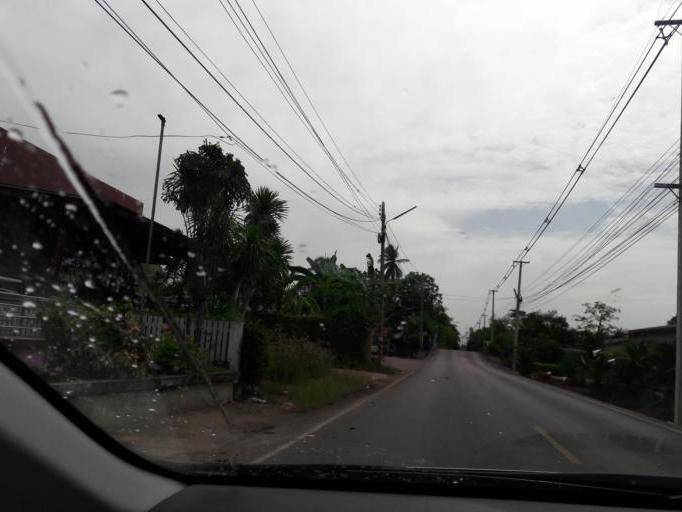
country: TH
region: Ratchaburi
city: Damnoen Saduak
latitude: 13.5368
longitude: 99.9957
